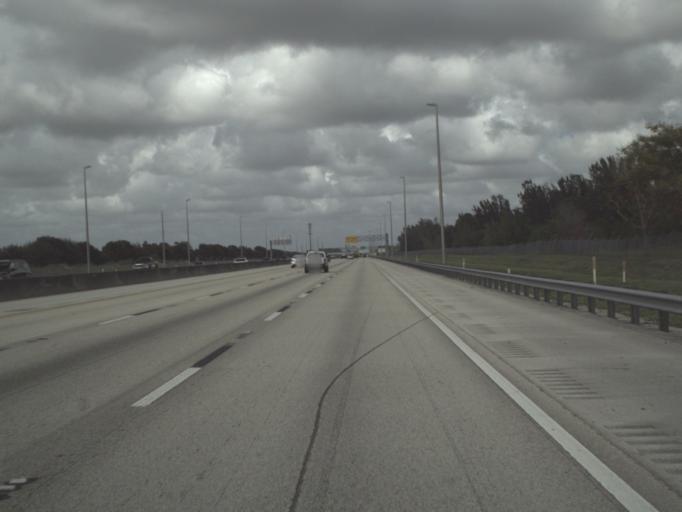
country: US
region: Florida
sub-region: Palm Beach County
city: Seminole Manor
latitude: 26.5455
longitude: -80.1727
